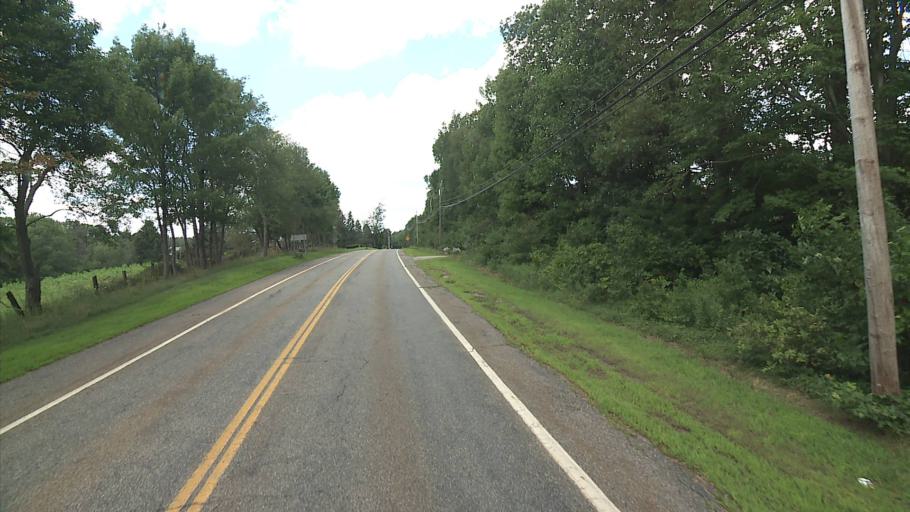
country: US
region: Connecticut
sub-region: Tolland County
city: Stafford
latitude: 41.9446
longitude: -72.1920
